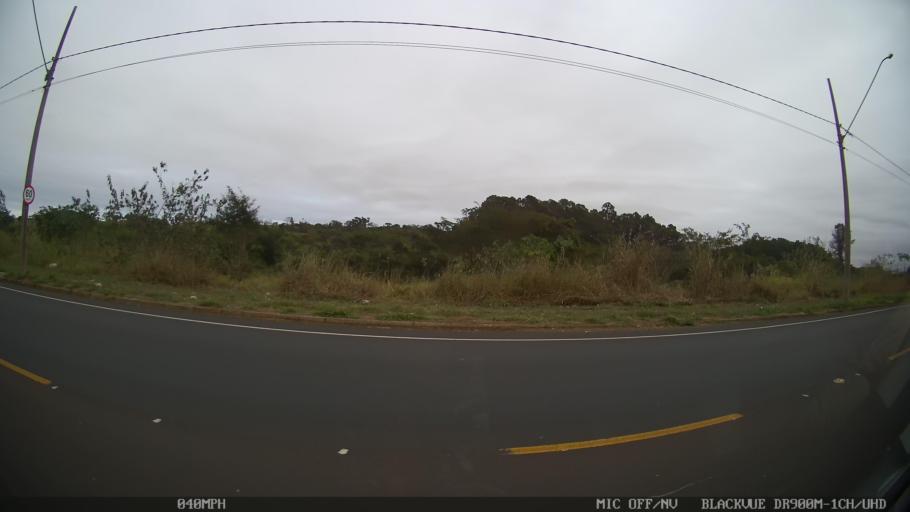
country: BR
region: Sao Paulo
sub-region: Sao Jose Do Rio Preto
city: Sao Jose do Rio Preto
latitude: -20.8203
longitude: -49.4359
